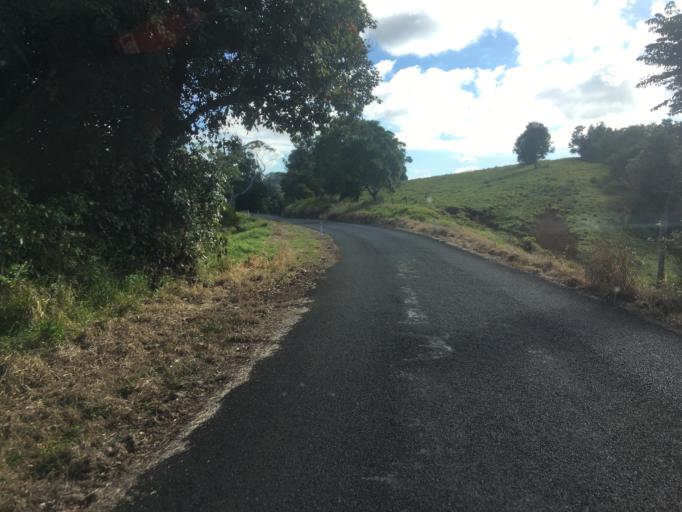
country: AU
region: Queensland
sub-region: Tablelands
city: Ravenshoe
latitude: -17.5860
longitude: 145.6036
